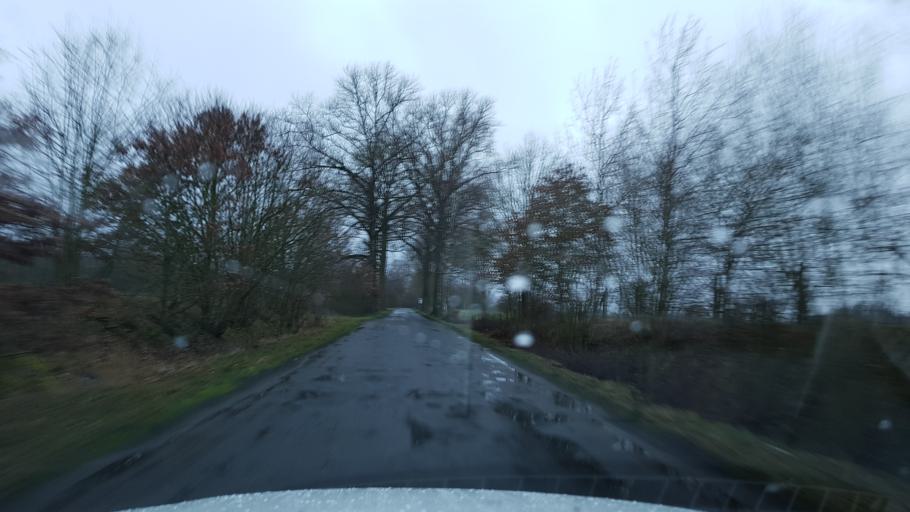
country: PL
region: West Pomeranian Voivodeship
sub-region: Powiat goleniowski
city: Nowogard
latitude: 53.5854
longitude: 15.1078
